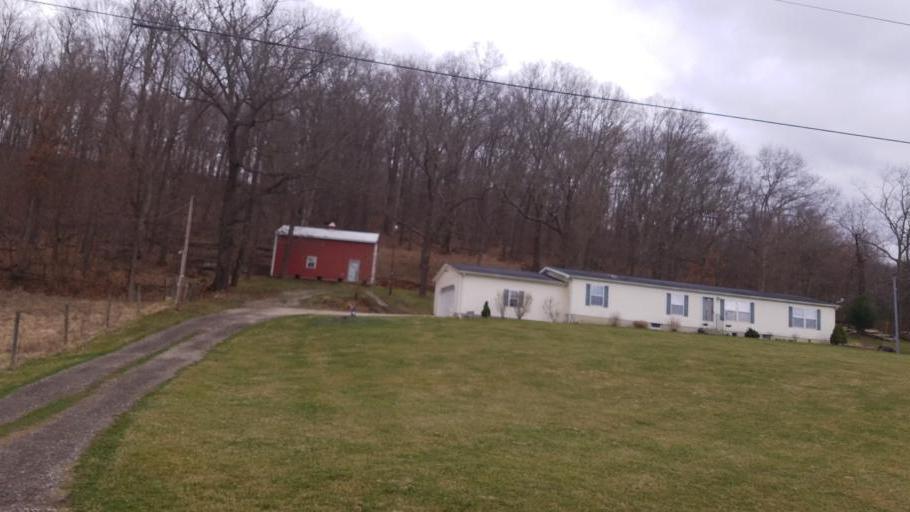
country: US
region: Ohio
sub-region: Licking County
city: Newark
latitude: 40.1570
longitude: -82.2930
